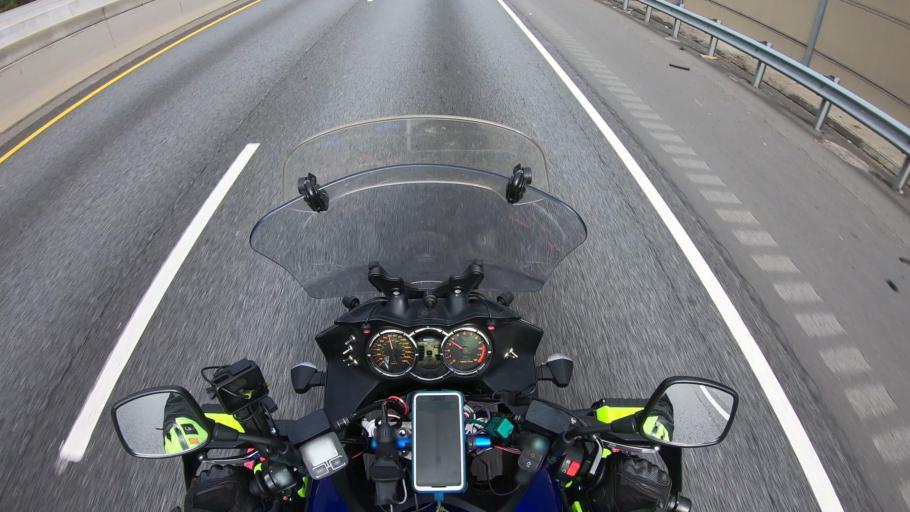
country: US
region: Georgia
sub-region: Cherokee County
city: Woodstock
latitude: 34.0621
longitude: -84.5380
